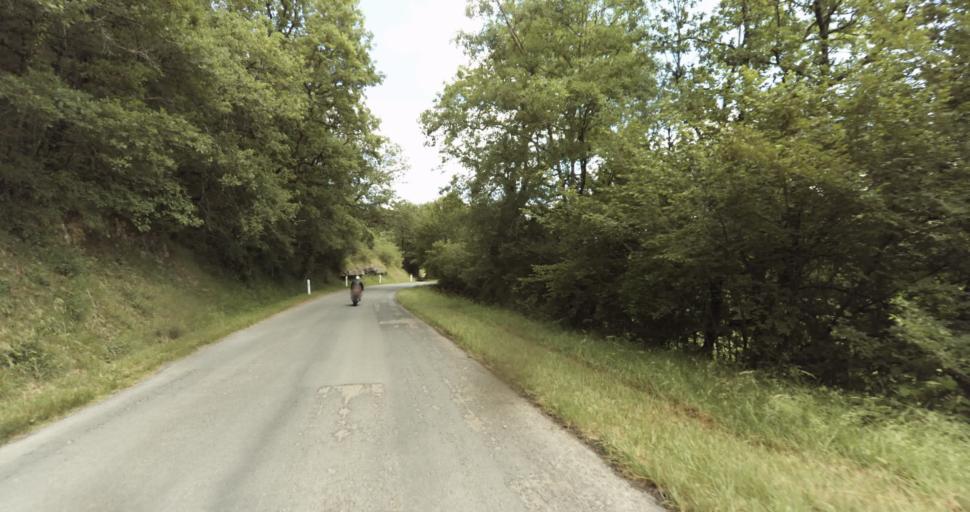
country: FR
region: Aquitaine
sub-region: Departement de la Dordogne
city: Beaumont-du-Perigord
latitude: 44.7588
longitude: 0.7315
